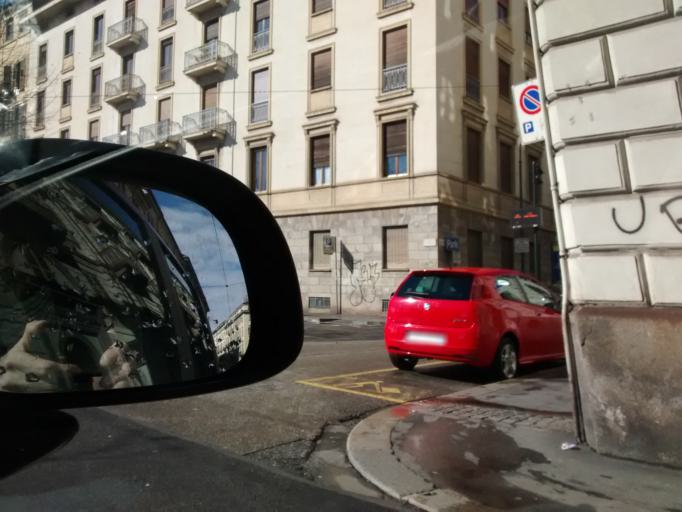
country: IT
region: Piedmont
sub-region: Provincia di Torino
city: Turin
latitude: 45.0629
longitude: 7.6941
